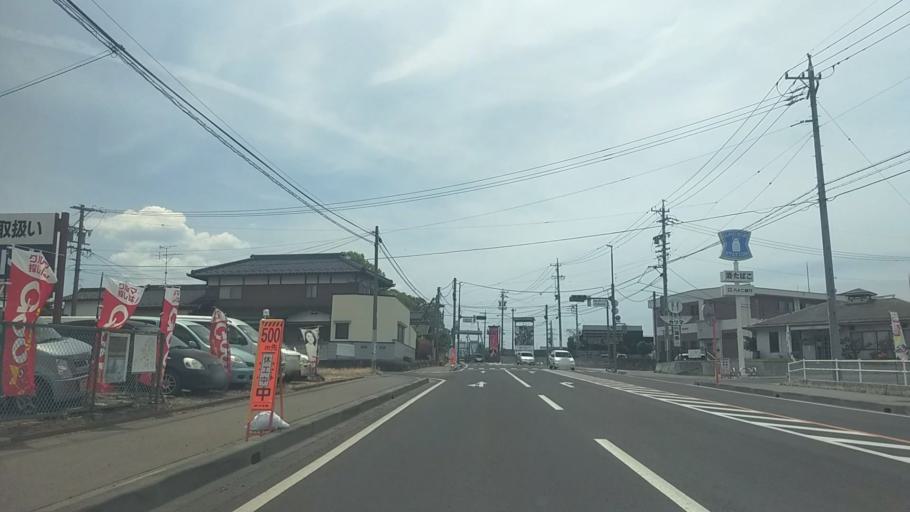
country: JP
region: Nagano
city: Saku
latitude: 36.1899
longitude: 138.4803
